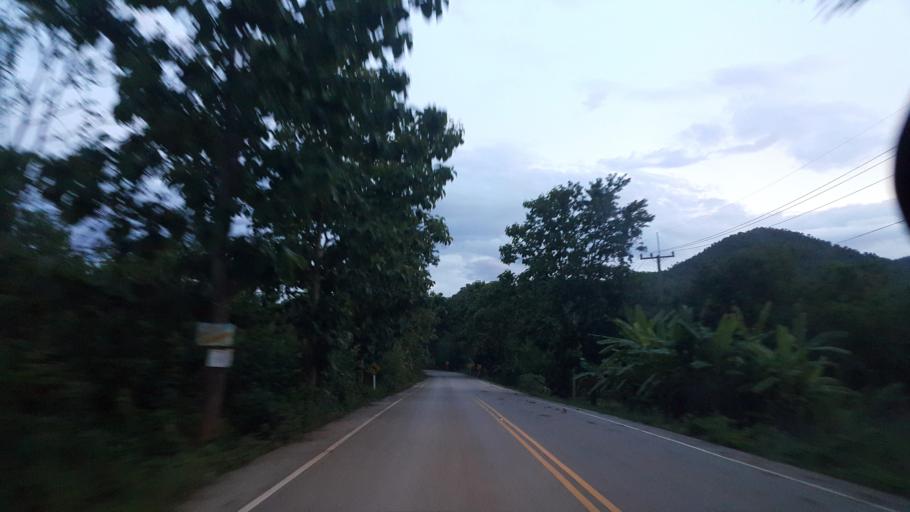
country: TH
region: Loei
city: Phu Ruea
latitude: 17.5332
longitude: 101.2280
